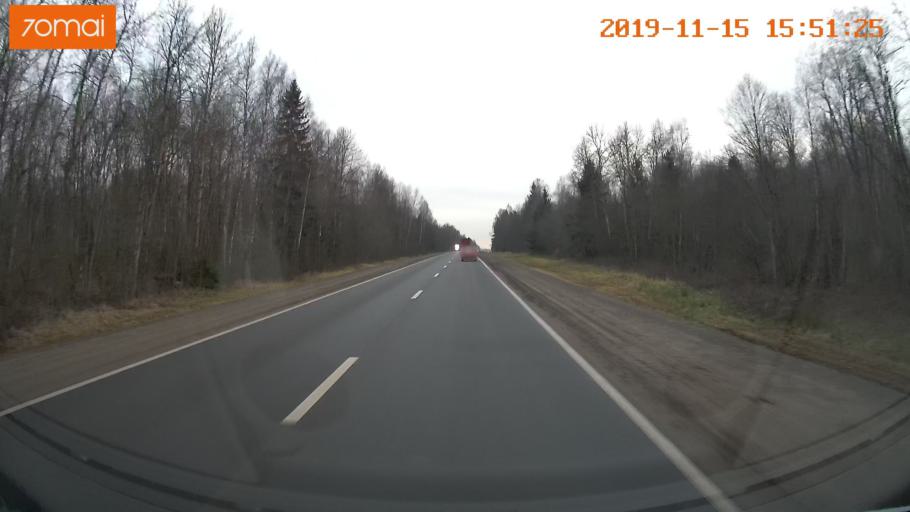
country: RU
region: Jaroslavl
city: Yaroslavl
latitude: 57.8946
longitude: 40.0076
